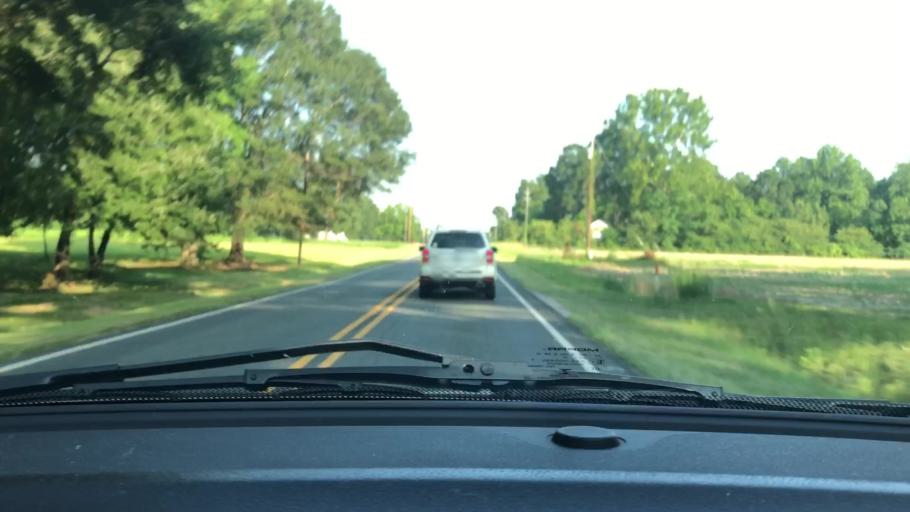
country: US
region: North Carolina
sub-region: Lee County
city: Broadway
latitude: 35.3529
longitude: -79.0752
